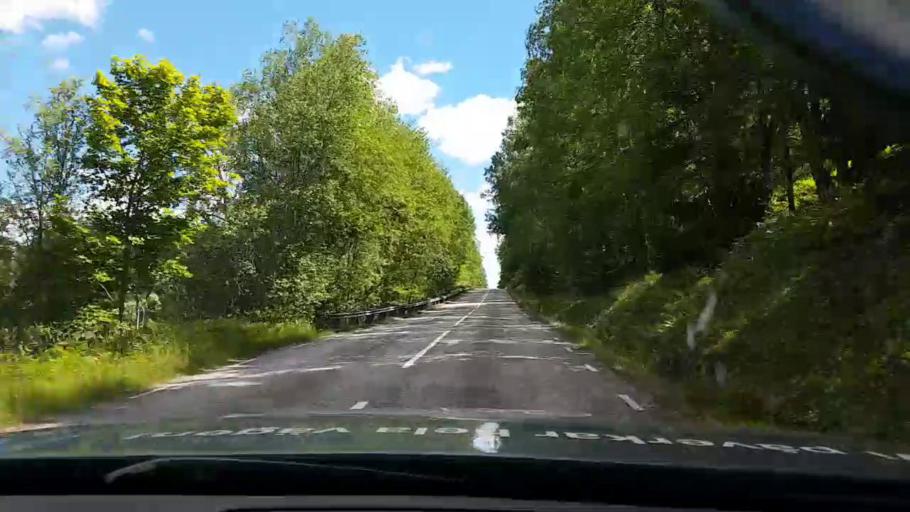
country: SE
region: Kalmar
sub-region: Vasterviks Kommun
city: Overum
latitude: 58.0709
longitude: 16.3811
